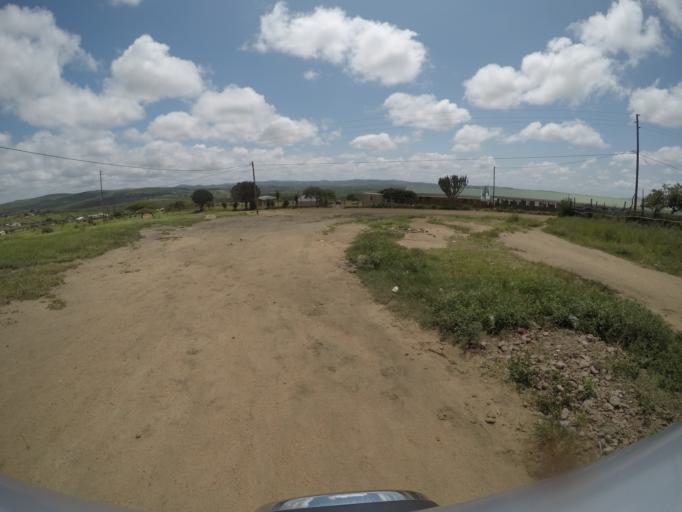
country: ZA
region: KwaZulu-Natal
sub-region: uThungulu District Municipality
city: Empangeni
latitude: -28.5774
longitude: 31.8424
